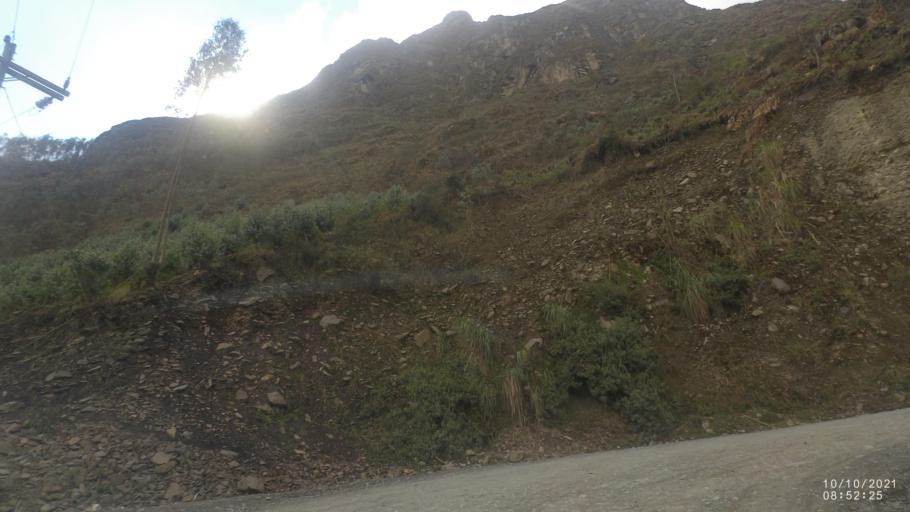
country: BO
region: La Paz
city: Quime
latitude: -16.9852
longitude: -67.2283
